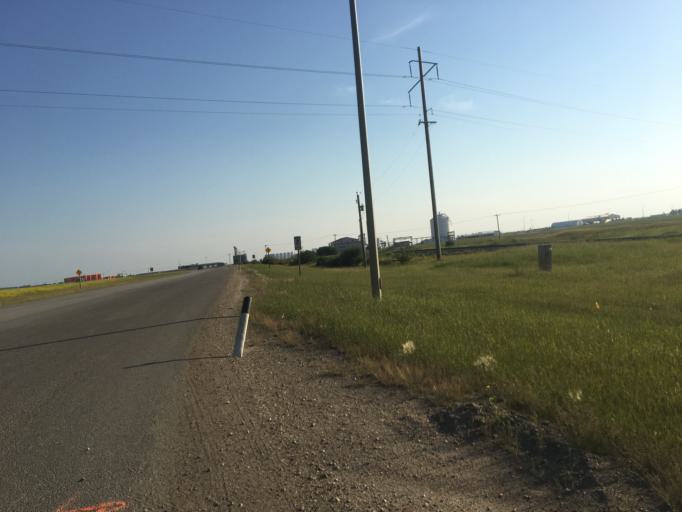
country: CA
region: Alberta
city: Sexsmith
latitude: 55.3163
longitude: -118.7925
